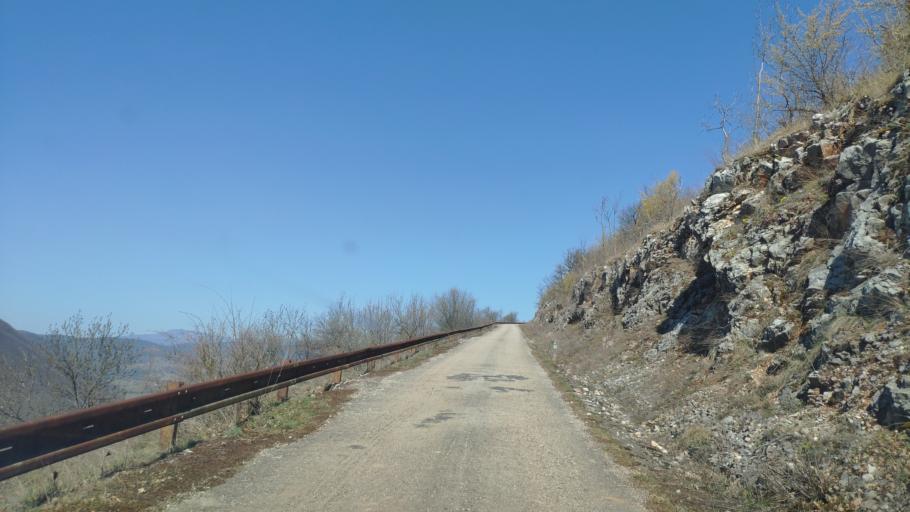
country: SK
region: Kosicky
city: Roznava
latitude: 48.5789
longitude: 20.4047
